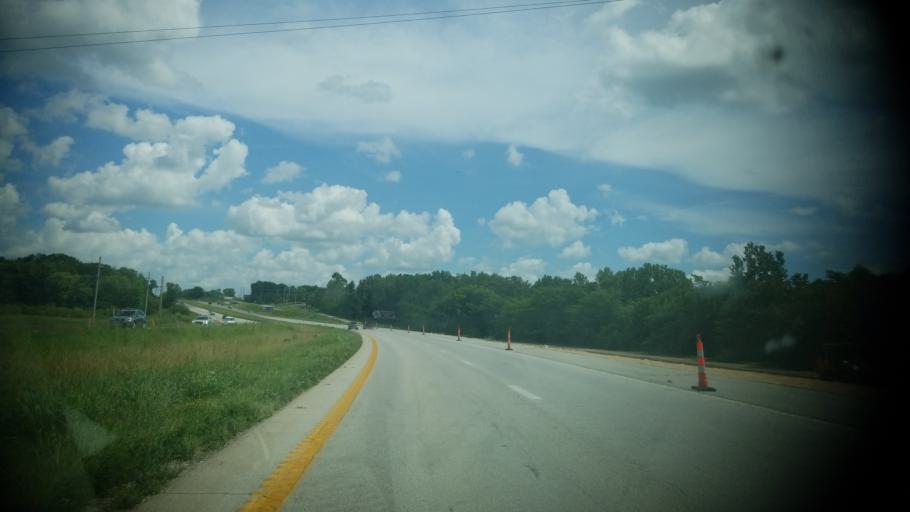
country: US
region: Missouri
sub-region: Lincoln County
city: Troy
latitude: 39.0069
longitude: -90.9777
